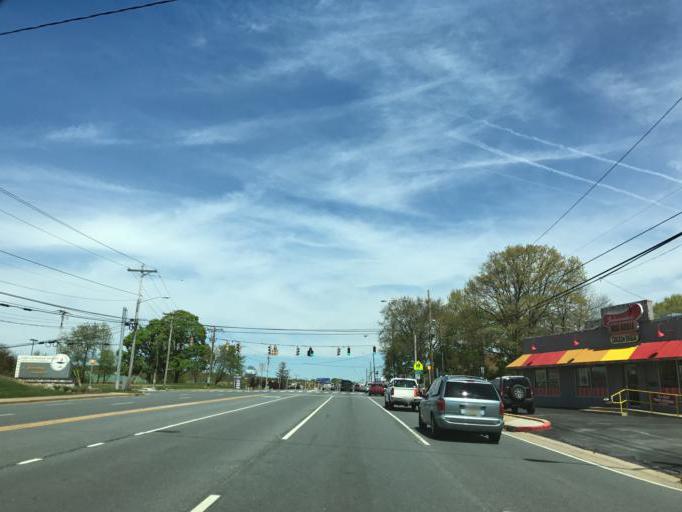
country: US
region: Delaware
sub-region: New Castle County
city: Bellefonte
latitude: 39.8019
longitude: -75.5481
